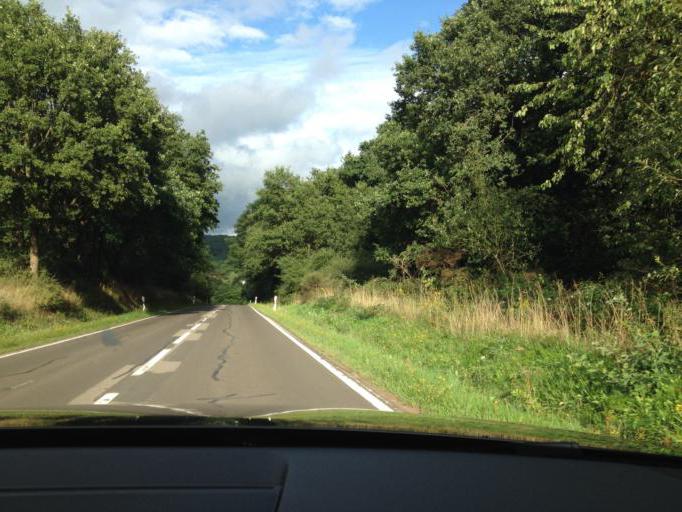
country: DE
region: Saarland
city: Namborn
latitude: 49.5213
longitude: 7.1205
